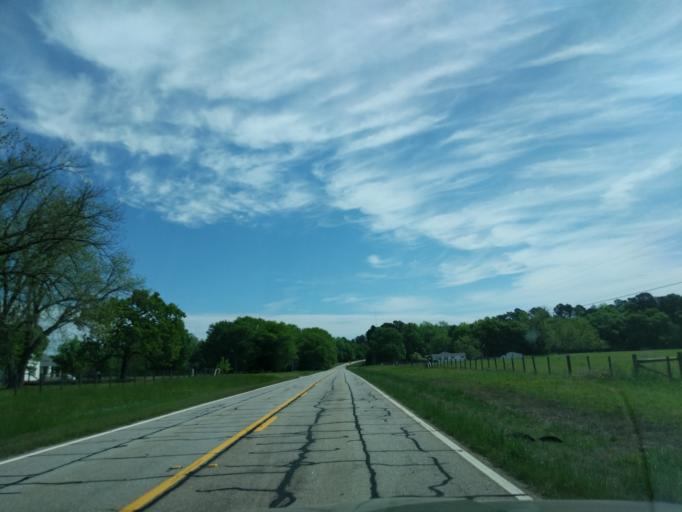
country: US
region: Georgia
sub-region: Columbia County
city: Appling
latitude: 33.6114
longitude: -82.3172
